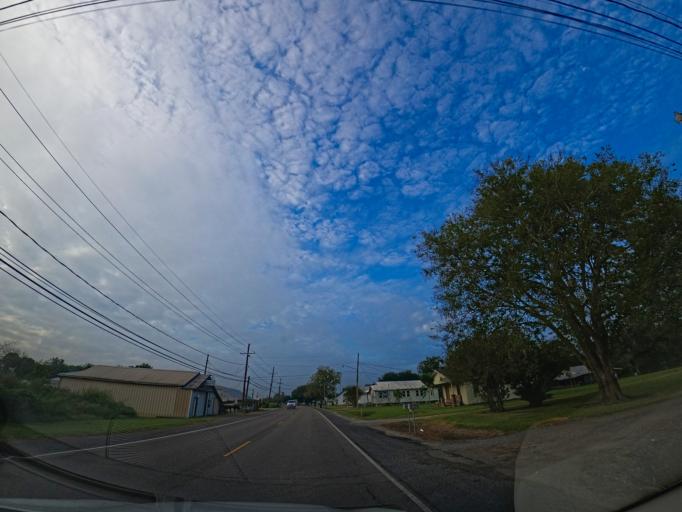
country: US
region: Louisiana
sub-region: Terrebonne Parish
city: Chauvin
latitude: 29.4496
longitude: -90.5932
